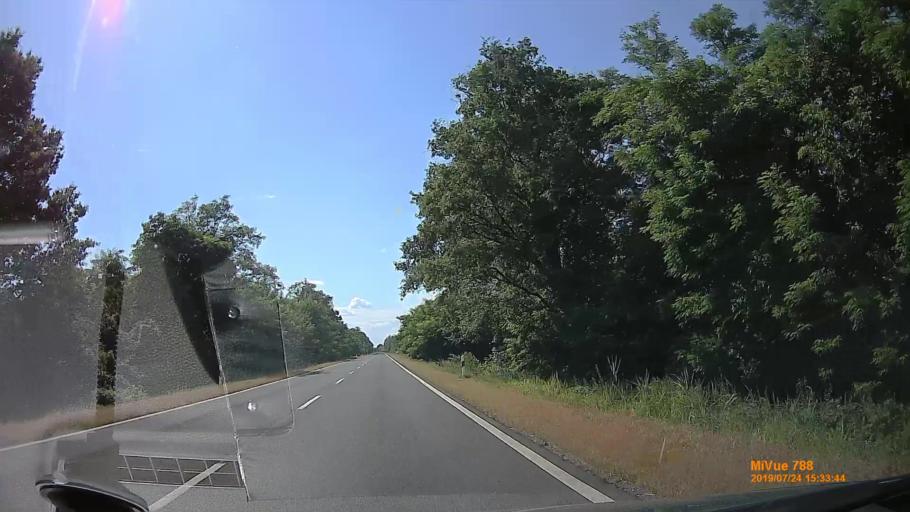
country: HU
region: Szabolcs-Szatmar-Bereg
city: Vasarosnameny
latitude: 48.1511
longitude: 22.3885
